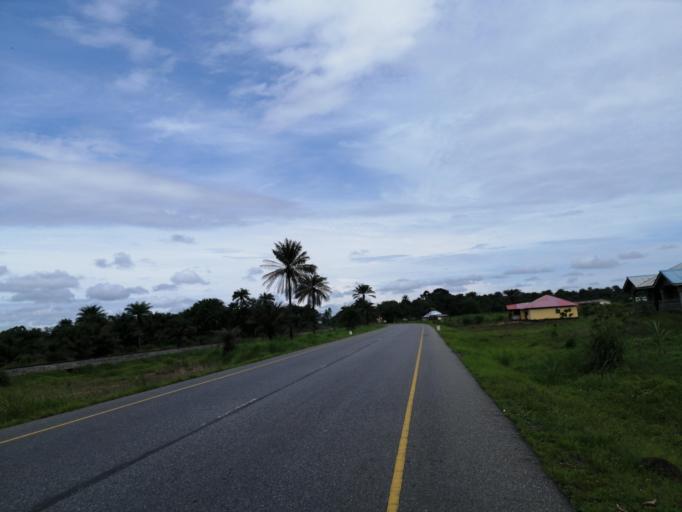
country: SL
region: Northern Province
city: Port Loko
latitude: 8.7435
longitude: -12.9344
